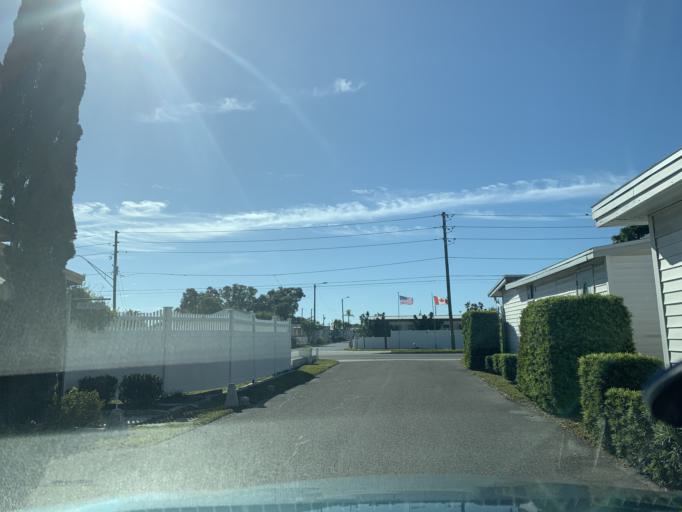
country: US
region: Florida
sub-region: Pinellas County
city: Kenneth City
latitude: 27.8140
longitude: -82.7426
